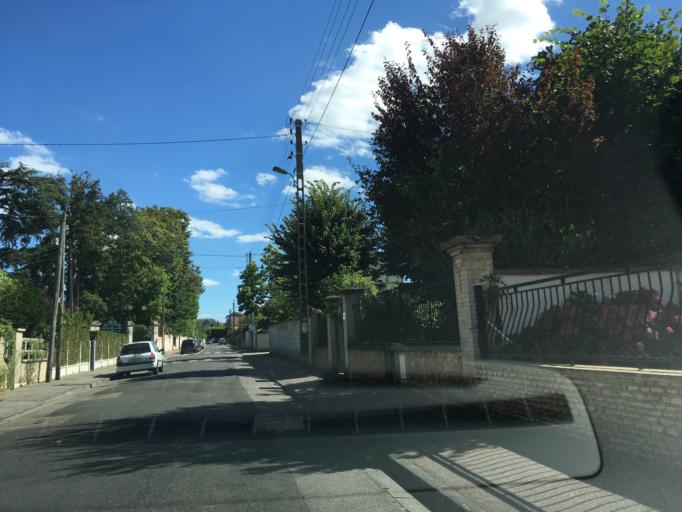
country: FR
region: Haute-Normandie
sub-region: Departement de l'Eure
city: Vernon
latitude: 49.0874
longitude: 1.4766
